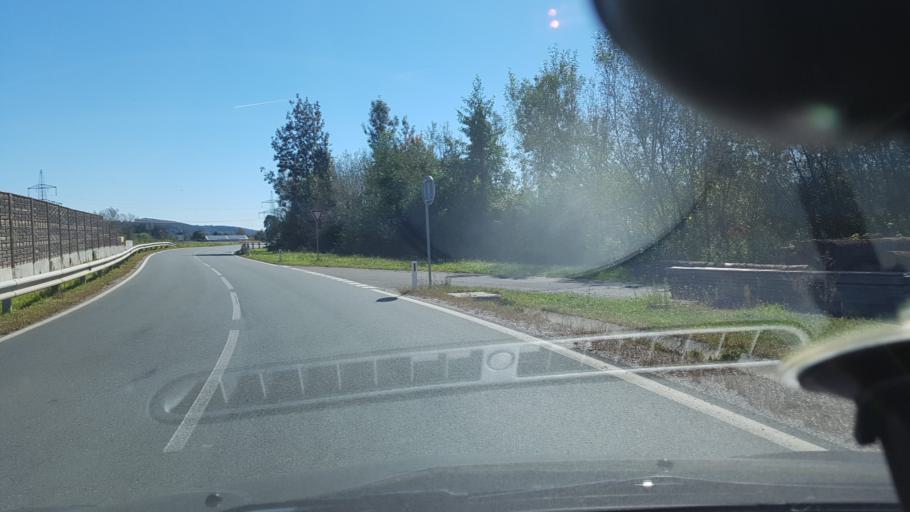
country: AT
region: Styria
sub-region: Politischer Bezirk Weiz
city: Oberrettenbach
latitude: 47.1415
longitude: 15.7858
